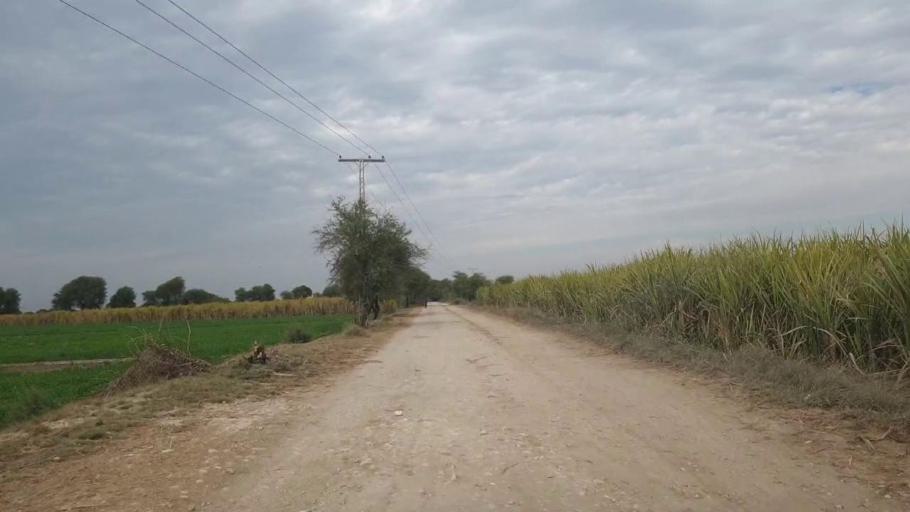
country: PK
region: Sindh
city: Jhol
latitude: 26.0197
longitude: 68.8750
